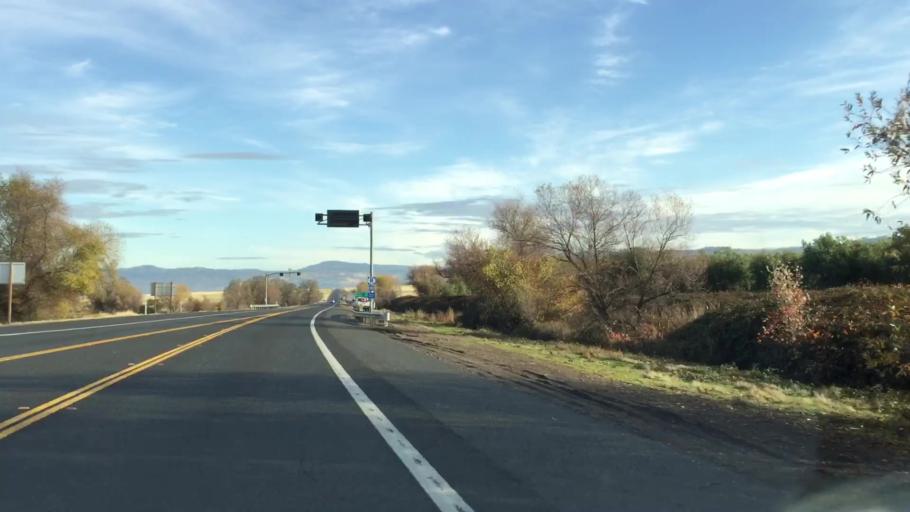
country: US
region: California
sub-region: Butte County
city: Thermalito
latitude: 39.6035
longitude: -121.6173
